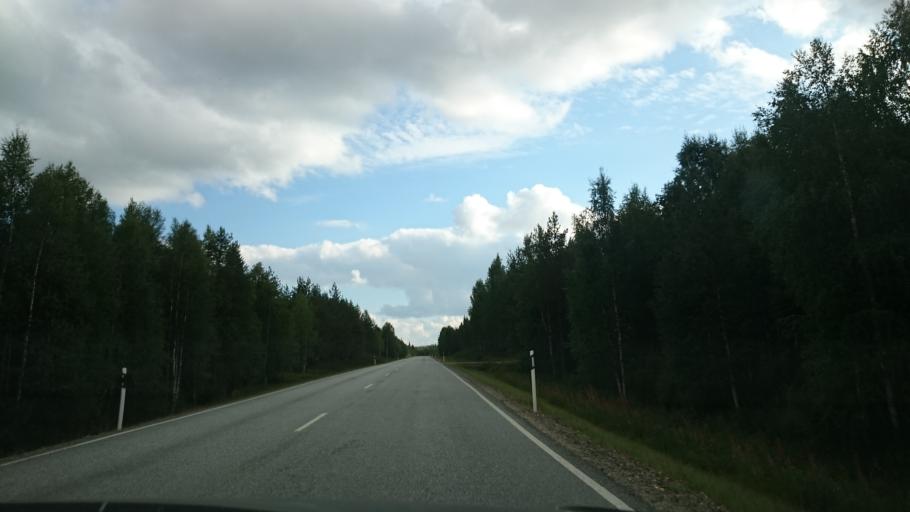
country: FI
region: Kainuu
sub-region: Kehys-Kainuu
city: Kuhmo
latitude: 64.5255
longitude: 29.9454
